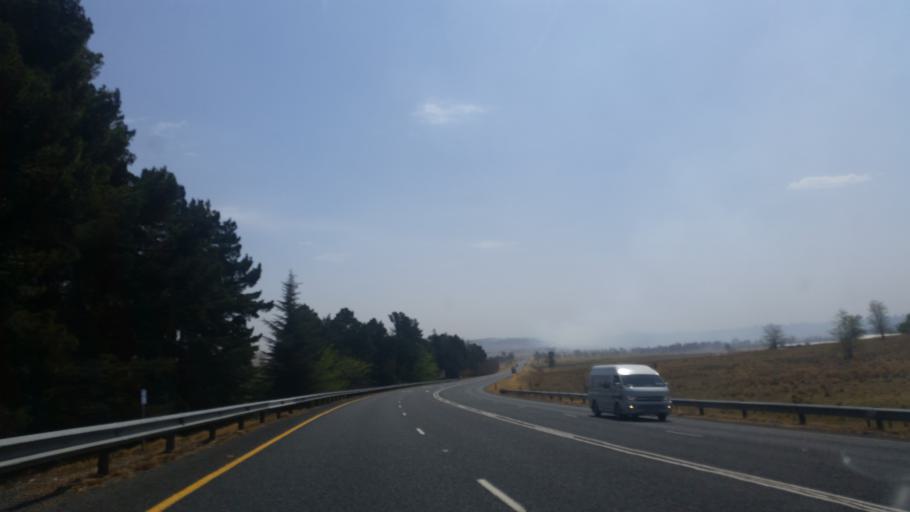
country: ZA
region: Orange Free State
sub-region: Thabo Mofutsanyana District Municipality
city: Bethlehem
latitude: -28.2885
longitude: 28.4073
